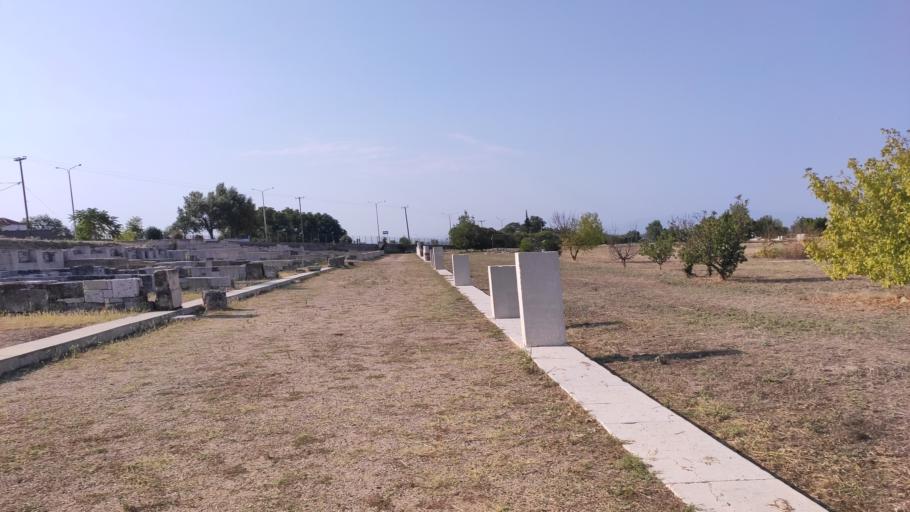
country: GR
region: Central Macedonia
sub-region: Nomos Pellis
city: Pella
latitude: 40.7564
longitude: 22.5203
